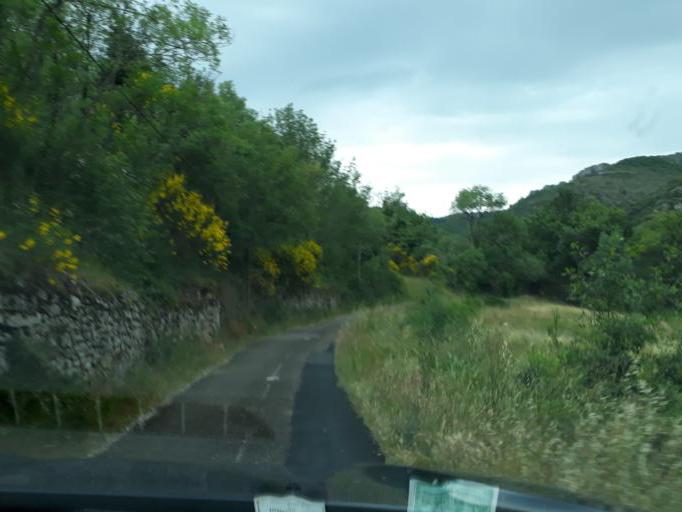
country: FR
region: Languedoc-Roussillon
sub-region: Departement de l'Herault
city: Lodeve
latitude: 43.7838
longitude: 3.2848
